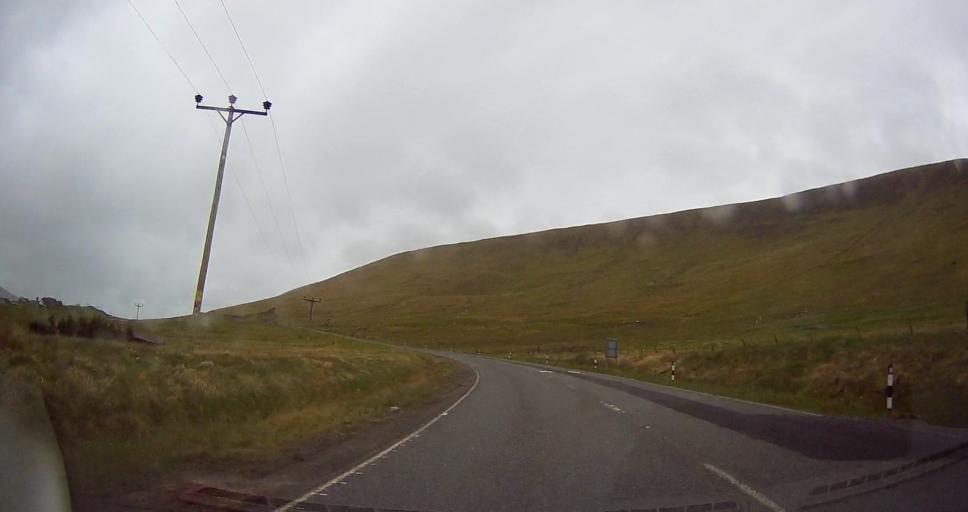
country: GB
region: Scotland
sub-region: Shetland Islands
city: Lerwick
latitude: 60.2542
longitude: -1.2961
